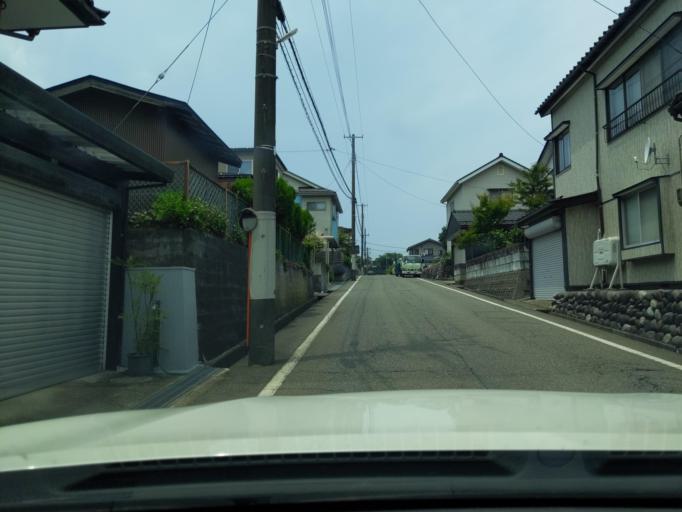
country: JP
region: Niigata
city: Kashiwazaki
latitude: 37.3532
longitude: 138.5430
